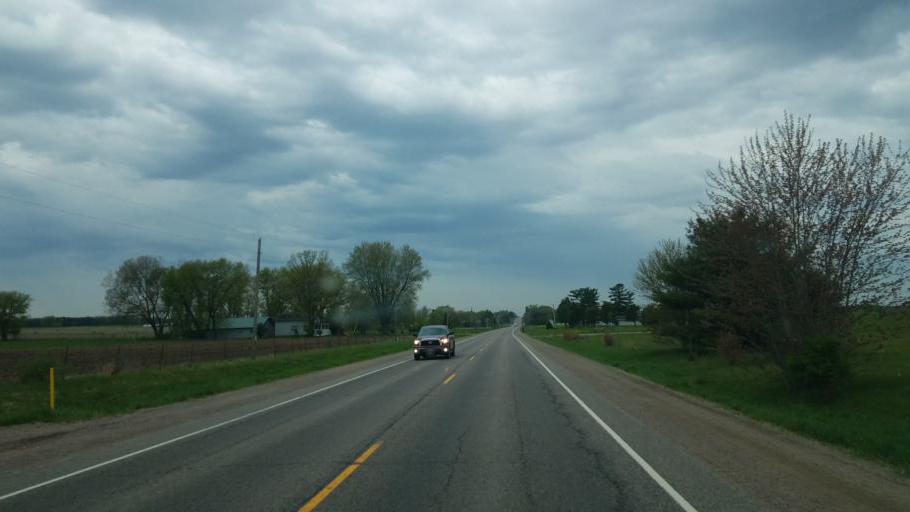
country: US
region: Wisconsin
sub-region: Marathon County
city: Spencer
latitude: 44.5983
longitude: -90.3439
